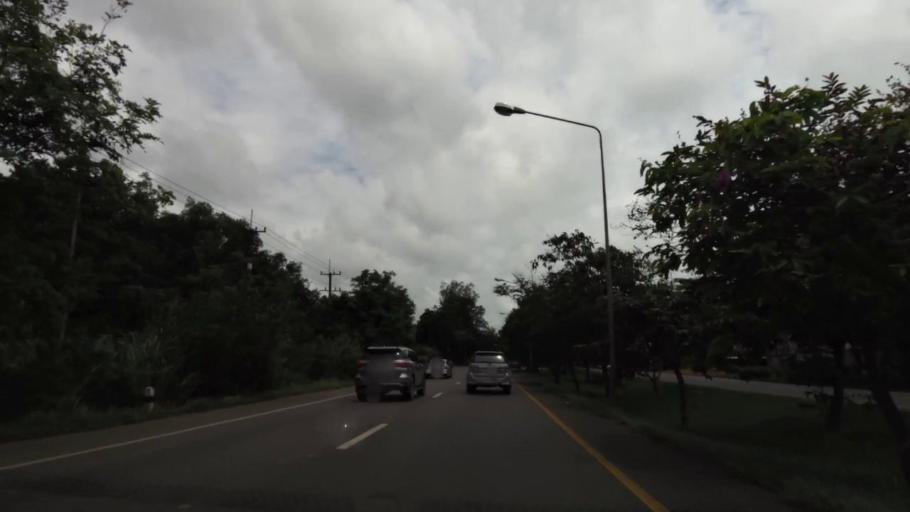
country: TH
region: Chanthaburi
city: Na Yai Am
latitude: 12.7386
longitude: 101.8930
